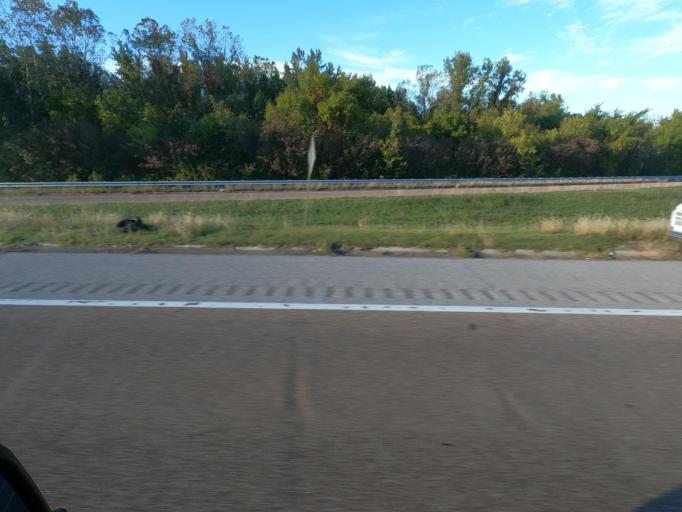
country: US
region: Tennessee
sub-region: Shelby County
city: Millington
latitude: 35.3305
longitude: -89.9020
